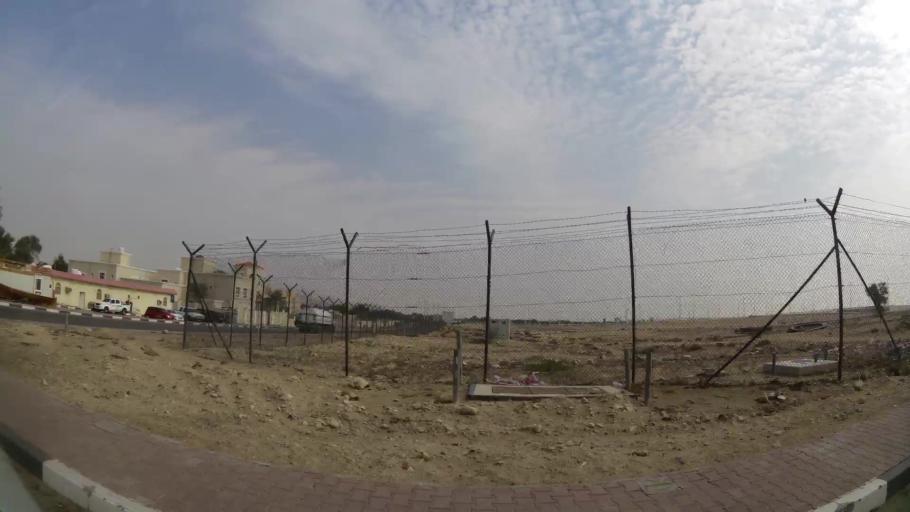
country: AE
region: Abu Dhabi
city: Abu Dhabi
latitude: 24.6854
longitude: 54.7685
